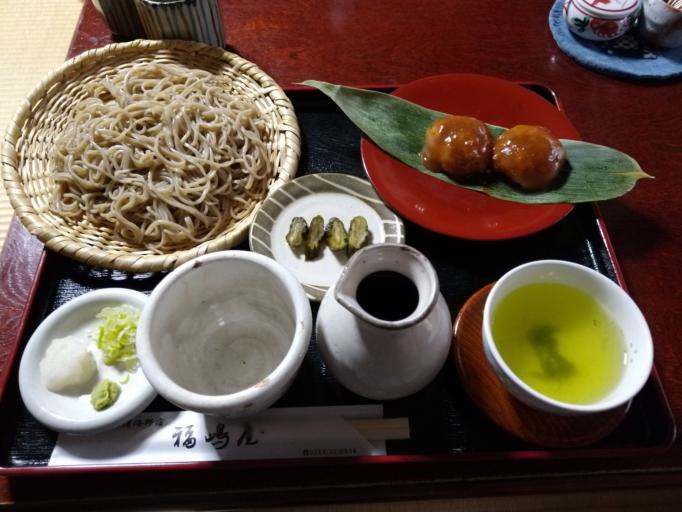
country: JP
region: Nagano
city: Ueda
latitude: 36.3606
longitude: 138.3154
